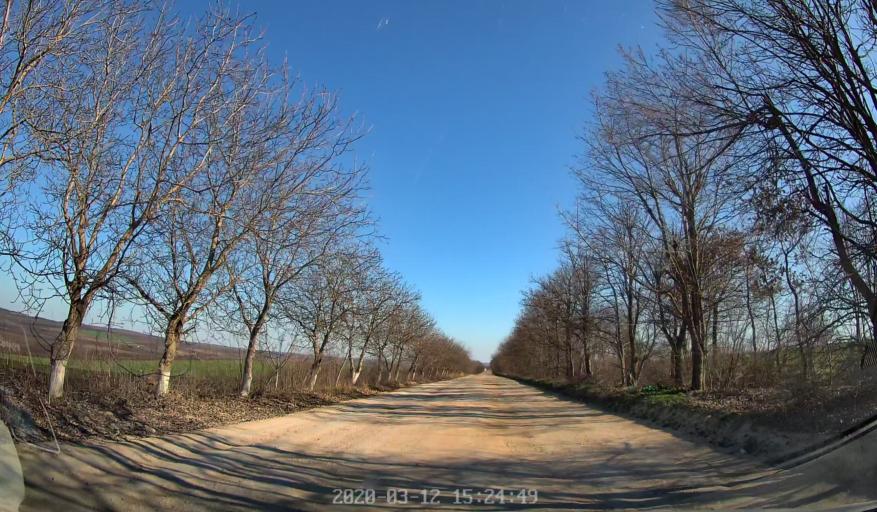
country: MD
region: Chisinau
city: Ciorescu
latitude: 47.1851
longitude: 28.9152
